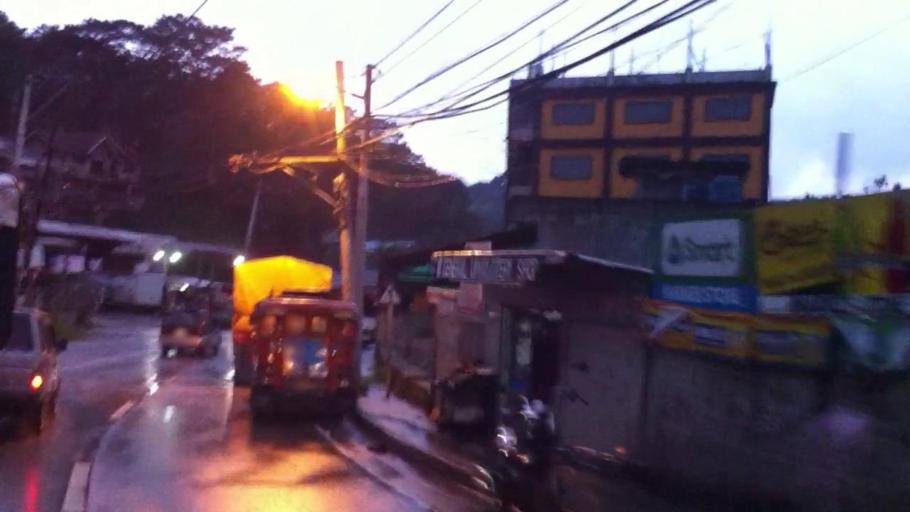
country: PH
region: Cordillera
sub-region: Province of Benguet
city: La Trinidad
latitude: 16.4448
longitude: 120.5811
